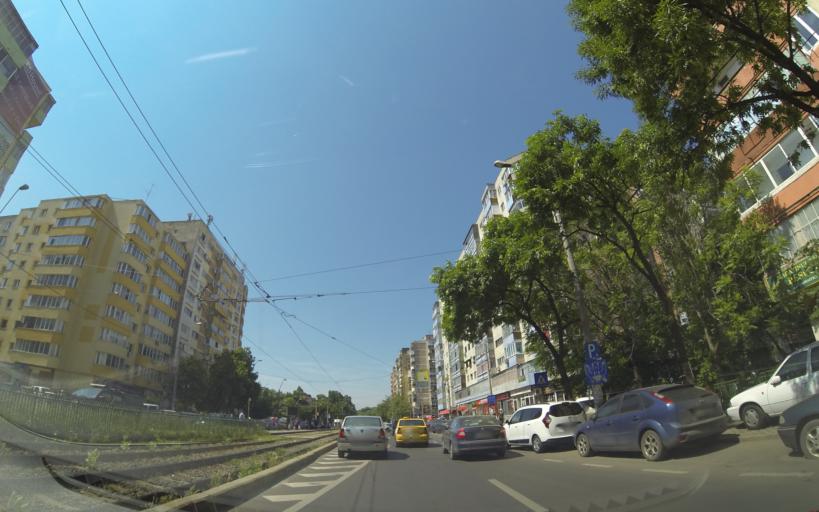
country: RO
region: Bucuresti
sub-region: Municipiul Bucuresti
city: Bucuresti
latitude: 44.4070
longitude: 26.0650
